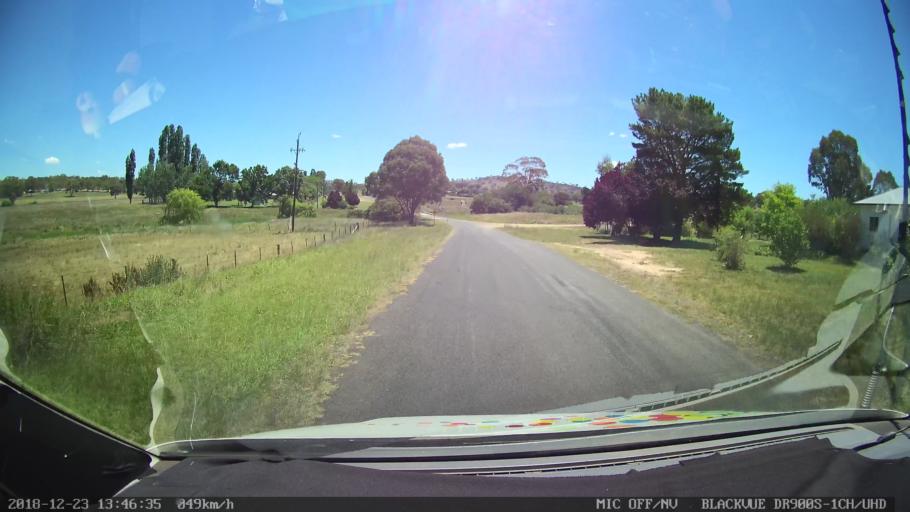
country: AU
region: New South Wales
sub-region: Tamworth Municipality
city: Manilla
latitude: -30.5054
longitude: 151.1181
